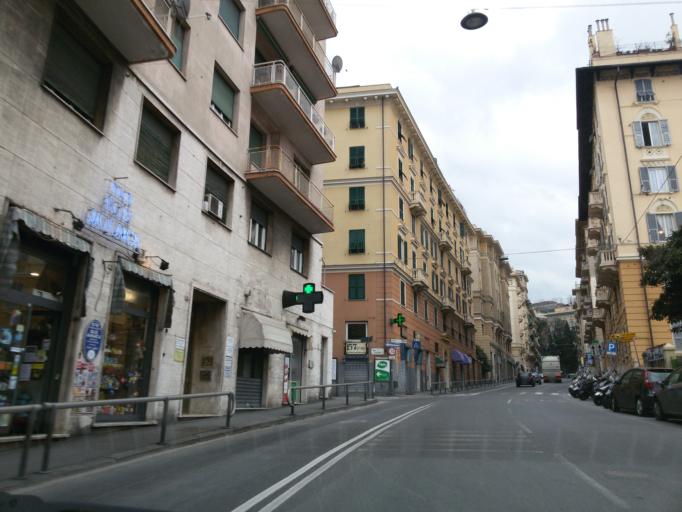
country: IT
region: Liguria
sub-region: Provincia di Genova
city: Genoa
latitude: 44.4069
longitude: 8.9648
